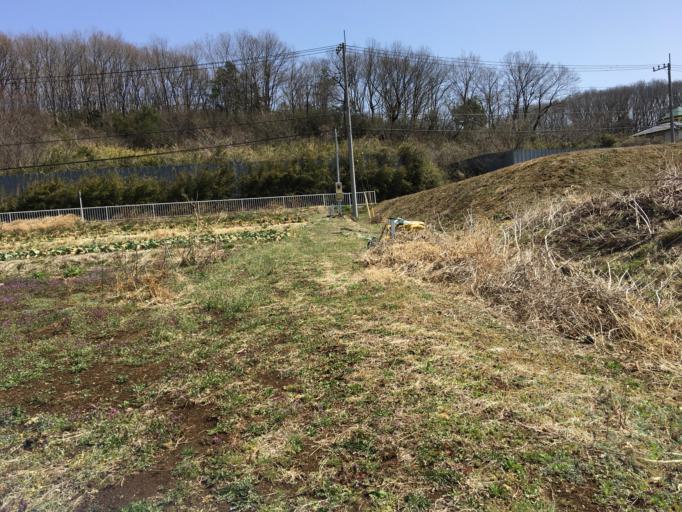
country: JP
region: Saitama
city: Sakado
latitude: 35.9987
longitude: 139.3338
